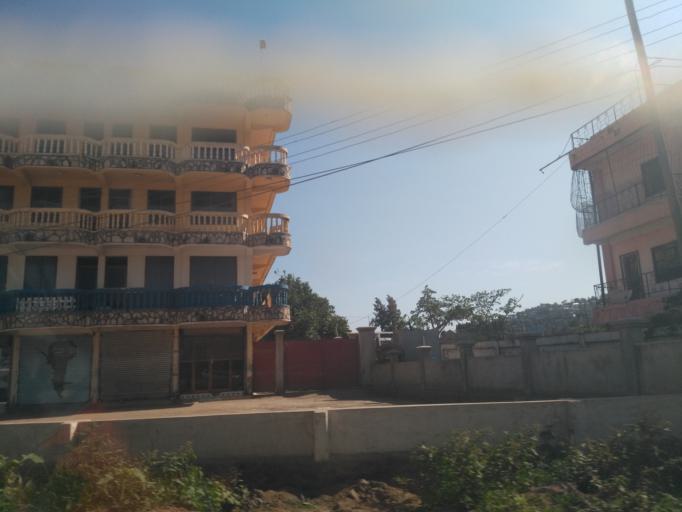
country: TZ
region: Mwanza
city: Mwanza
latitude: -2.5063
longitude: 32.8990
